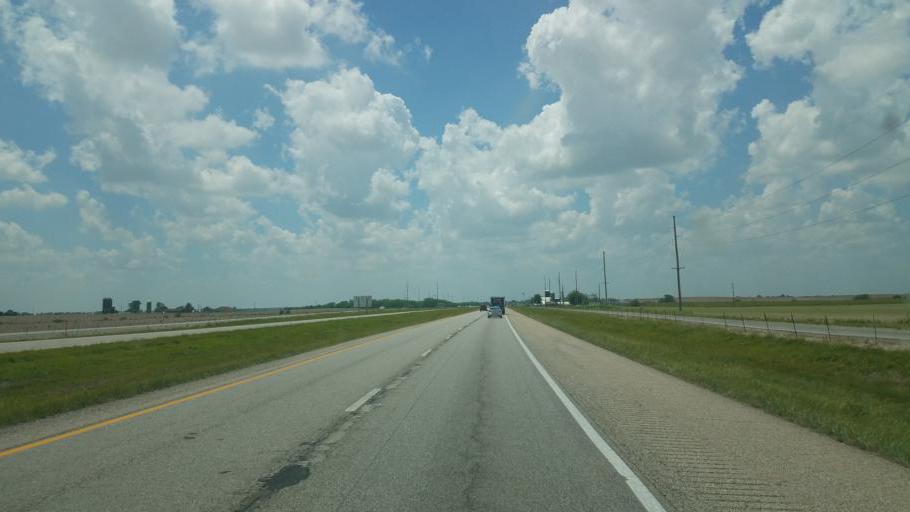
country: US
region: Illinois
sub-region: Madison County
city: Highland
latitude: 38.8151
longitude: -89.5682
